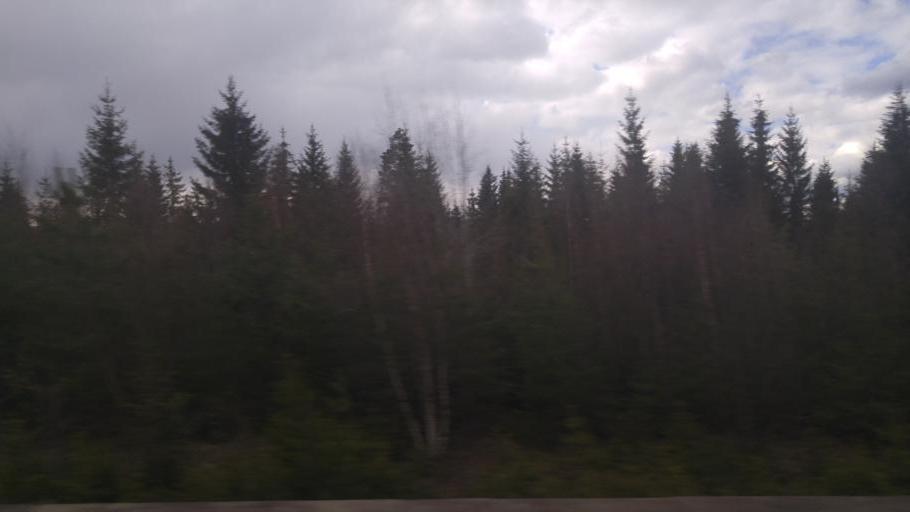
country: NO
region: Akershus
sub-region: Eidsvoll
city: Raholt
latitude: 60.2546
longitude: 11.1298
